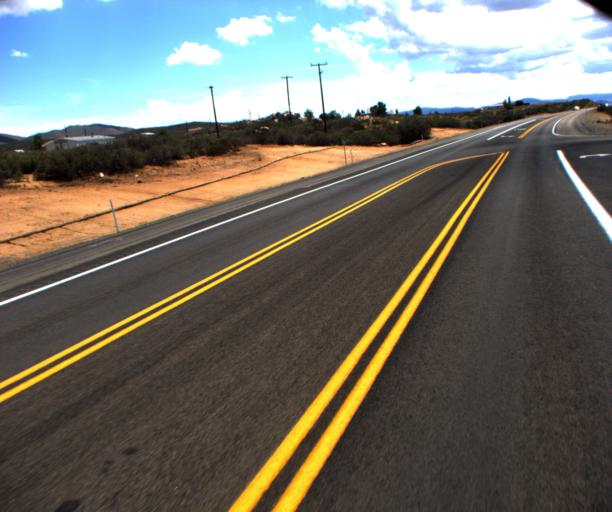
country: US
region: Arizona
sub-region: Yavapai County
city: Dewey-Humboldt
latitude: 34.5461
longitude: -112.1595
